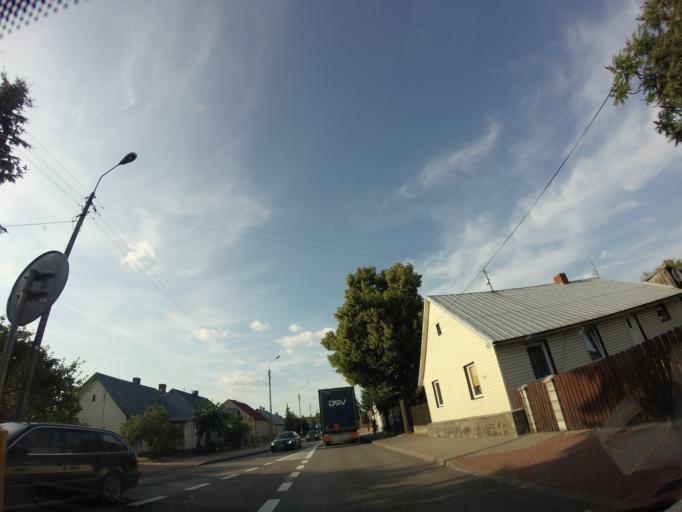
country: PL
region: Podlasie
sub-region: Powiat sokolski
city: Suchowola
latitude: 53.5834
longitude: 23.1072
